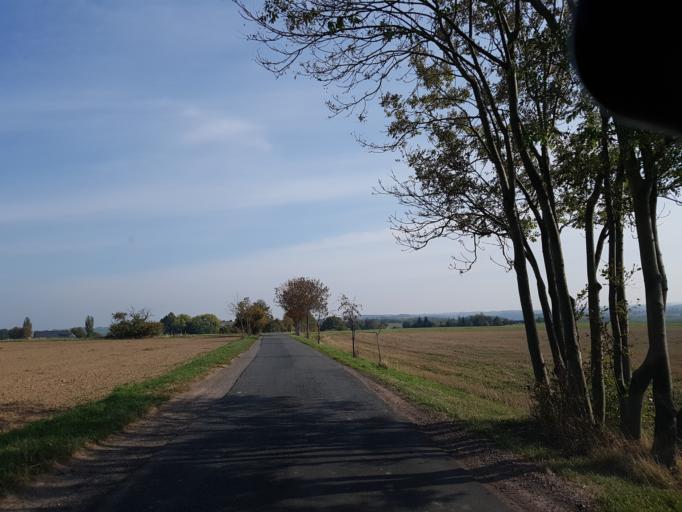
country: DE
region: Saxony
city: Hartha
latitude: 51.0927
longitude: 12.9940
